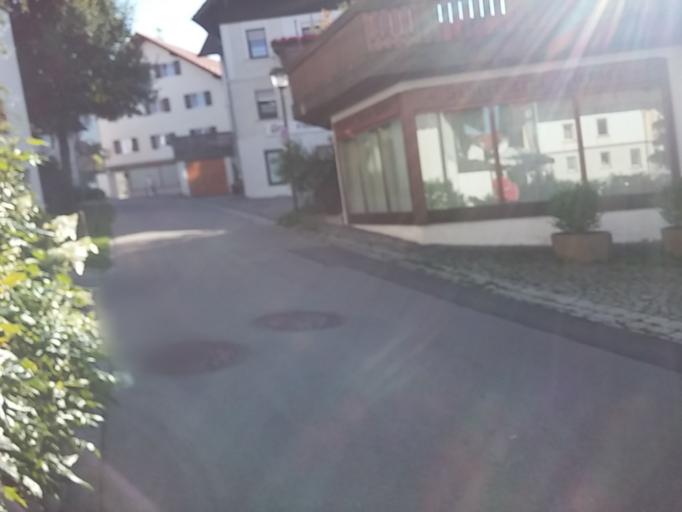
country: DE
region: Bavaria
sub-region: Swabia
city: Wiggensbach
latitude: 47.7448
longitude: 10.2312
